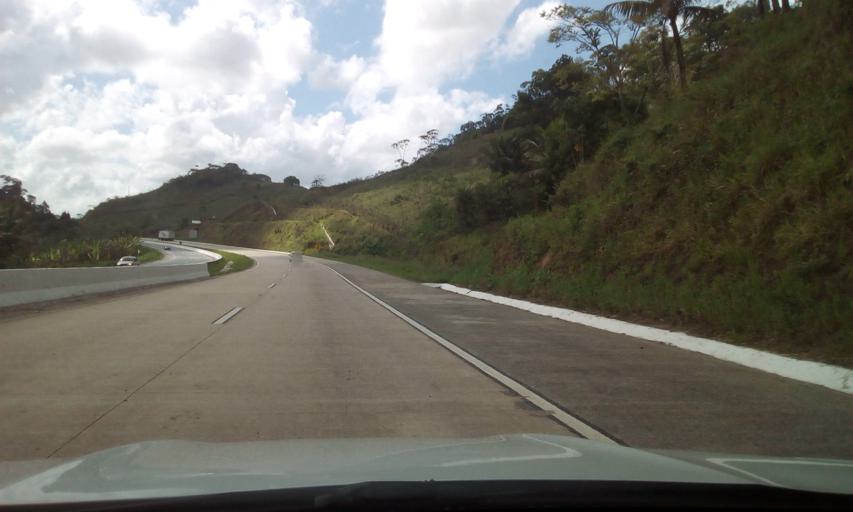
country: BR
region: Pernambuco
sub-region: Palmares
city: Palmares
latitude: -8.7411
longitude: -35.6083
